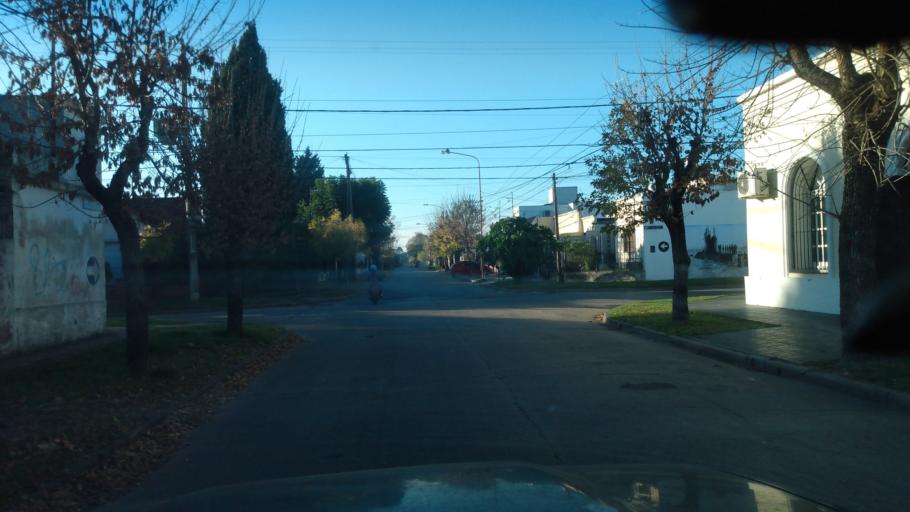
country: AR
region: Buenos Aires
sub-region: Partido de Lujan
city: Lujan
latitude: -34.5644
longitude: -59.1032
